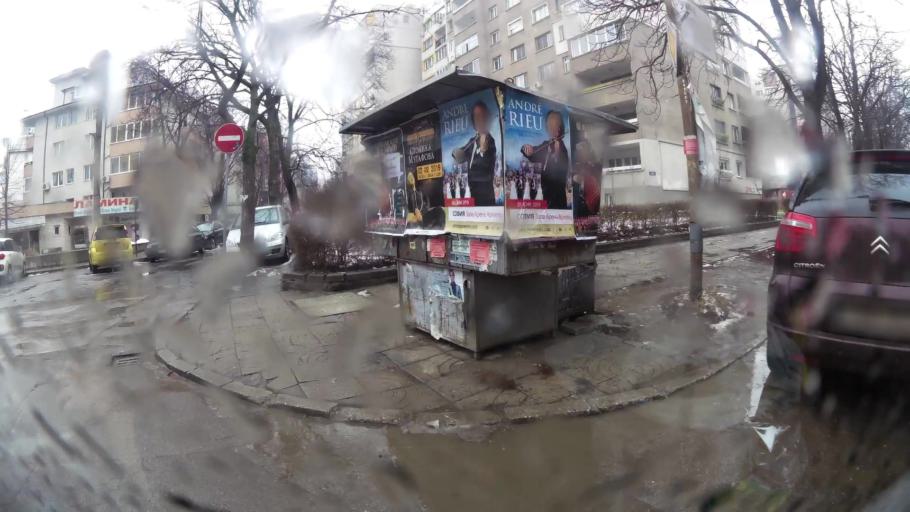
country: BG
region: Sofia-Capital
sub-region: Stolichna Obshtina
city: Sofia
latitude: 42.6699
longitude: 23.3026
